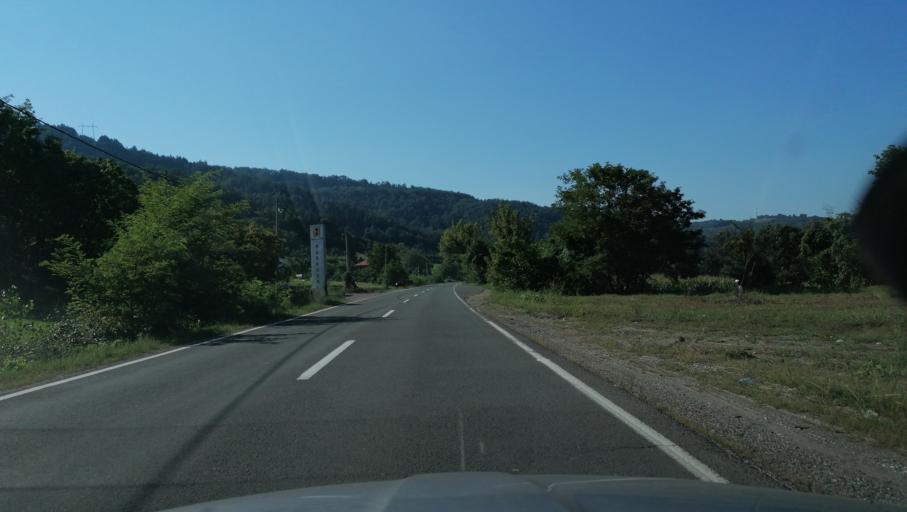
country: RS
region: Central Serbia
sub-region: Raski Okrug
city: Kraljevo
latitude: 43.6703
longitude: 20.5792
